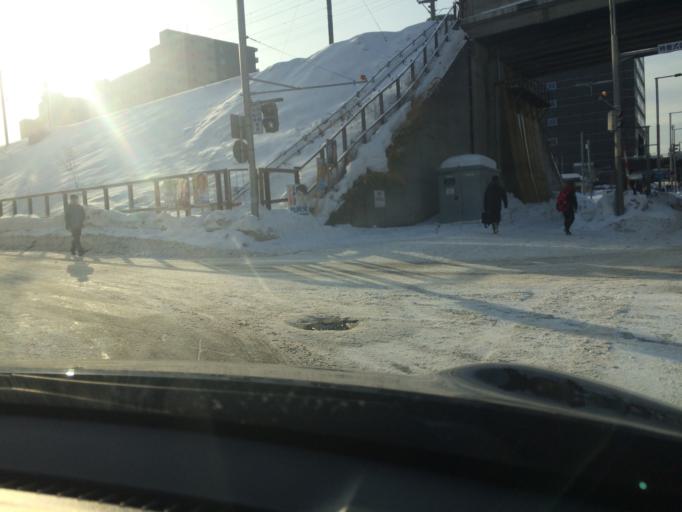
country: JP
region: Hokkaido
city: Ebetsu
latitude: 43.0387
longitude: 141.4740
